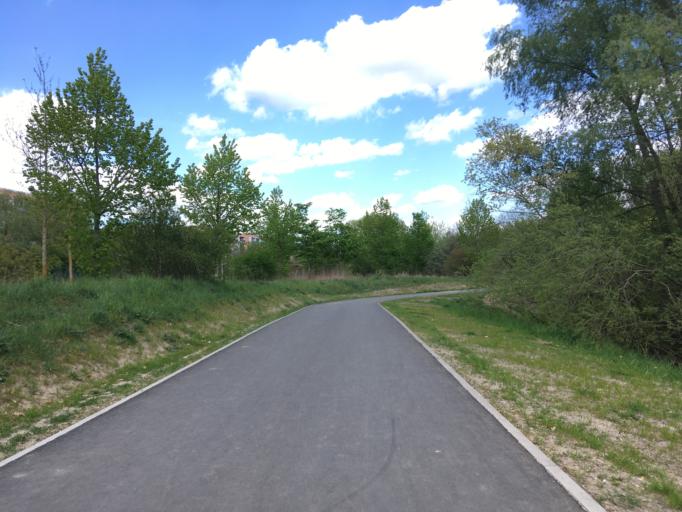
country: DE
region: Berlin
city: Hellersdorf
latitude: 52.5382
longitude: 13.6150
